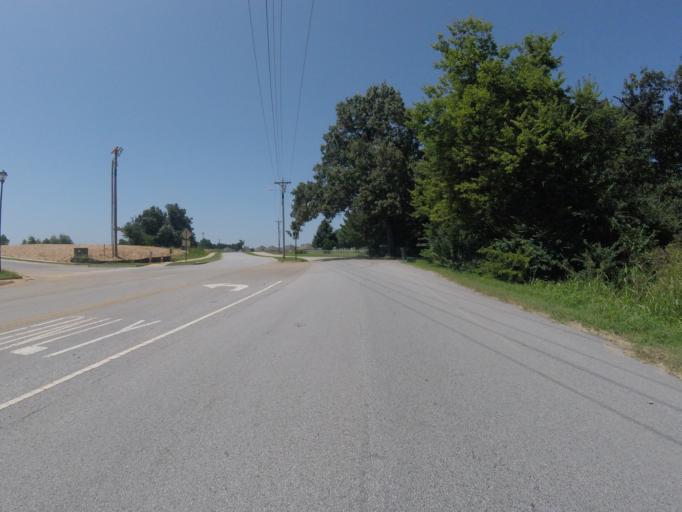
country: US
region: Arkansas
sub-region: Washington County
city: Farmington
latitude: 36.0875
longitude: -94.2162
